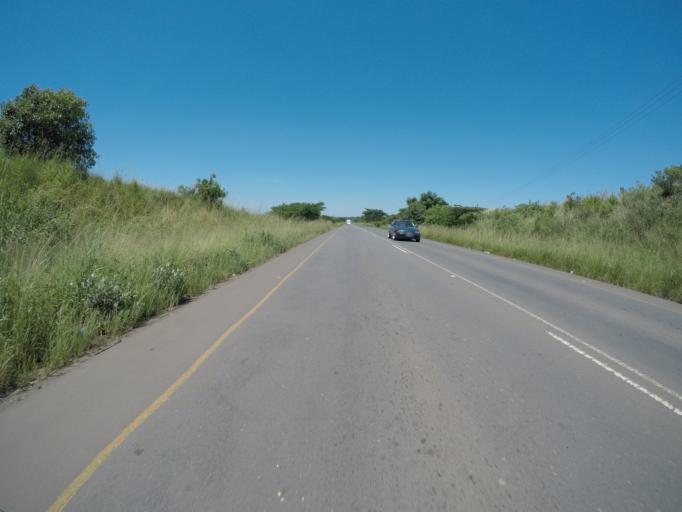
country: ZA
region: KwaZulu-Natal
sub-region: uThungulu District Municipality
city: Empangeni
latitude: -28.7311
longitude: 31.8731
